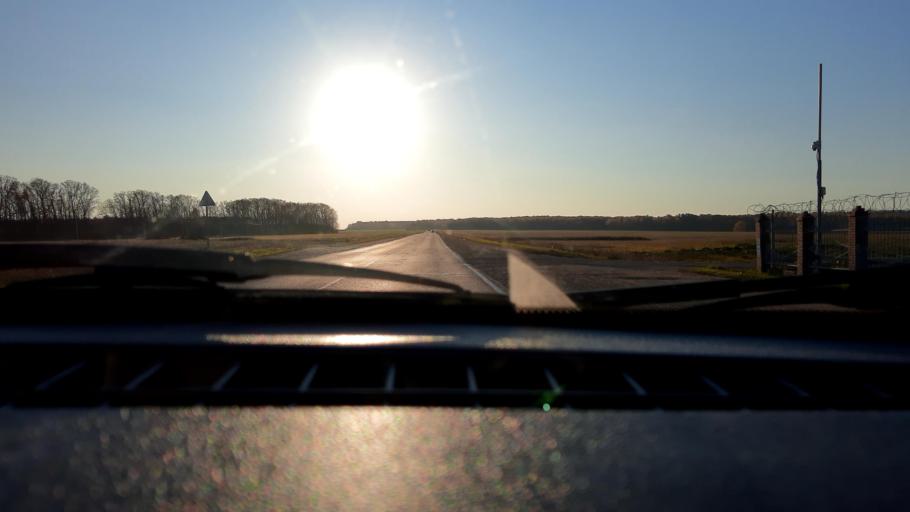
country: RU
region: Bashkortostan
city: Mikhaylovka
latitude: 54.8234
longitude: 55.7631
